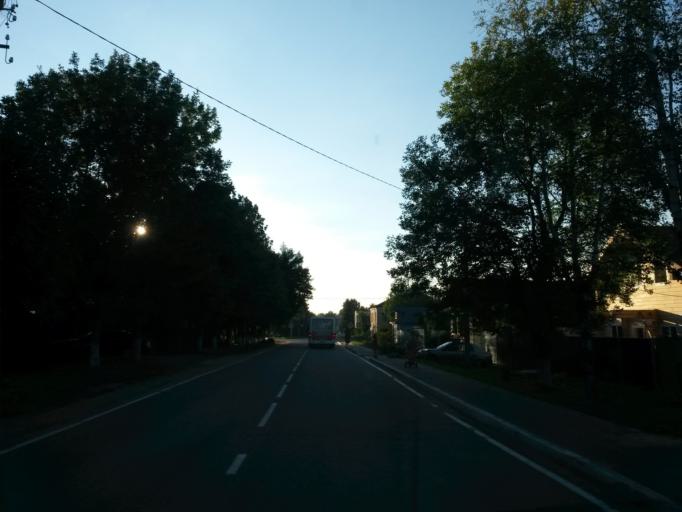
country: RU
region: Jaroslavl
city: Tutayev
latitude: 57.8726
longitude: 39.5263
